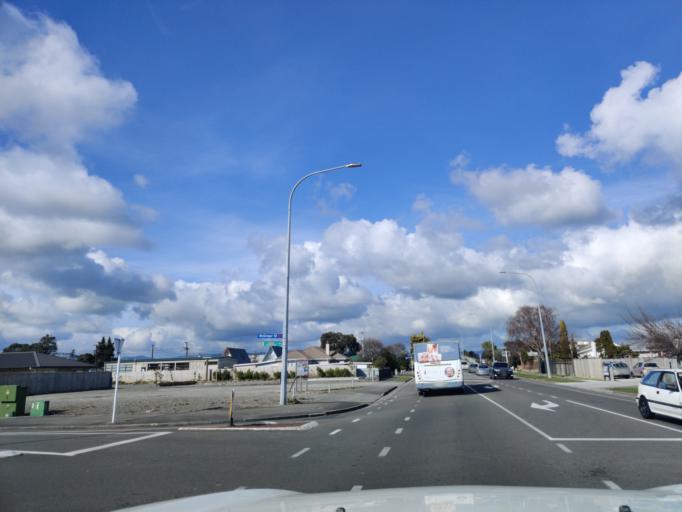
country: NZ
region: Manawatu-Wanganui
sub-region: Palmerston North City
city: Palmerston North
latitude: -40.3318
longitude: 175.6153
